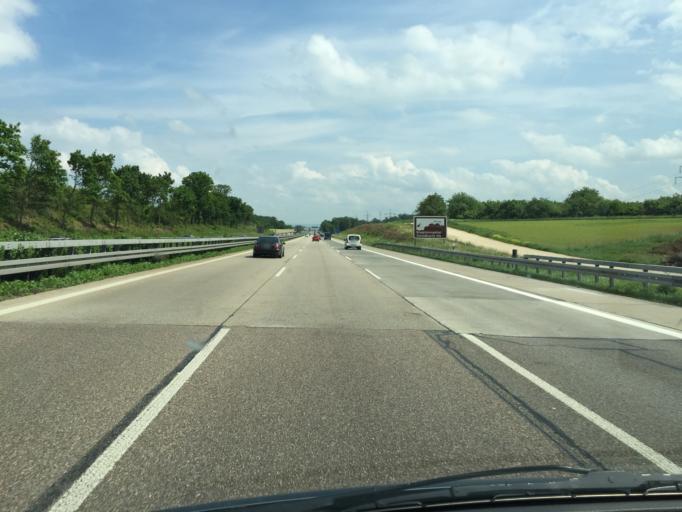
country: DE
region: Baden-Wuerttemberg
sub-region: Regierungsbezirk Stuttgart
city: Denkendorf
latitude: 48.6888
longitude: 9.3151
